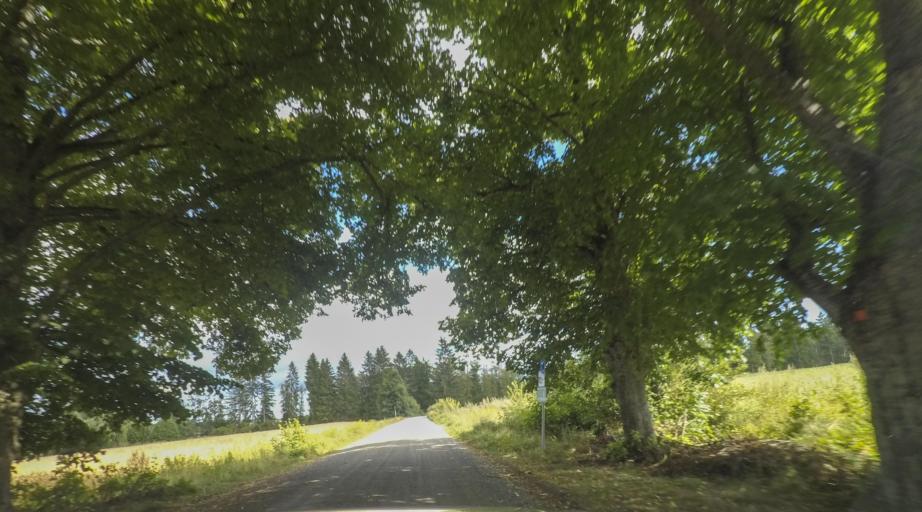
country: SE
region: Stockholm
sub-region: Sodertalje Kommun
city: Pershagen
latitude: 59.1068
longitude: 17.6766
